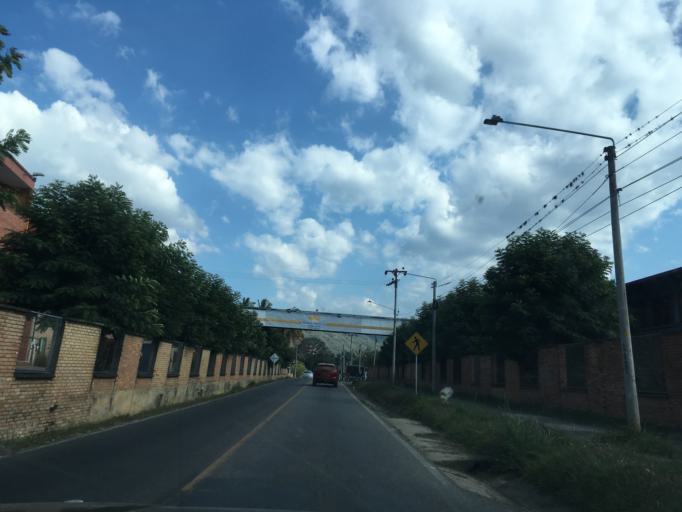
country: CO
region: Santander
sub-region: San Gil
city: San Gil
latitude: 6.5643
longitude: -73.1436
